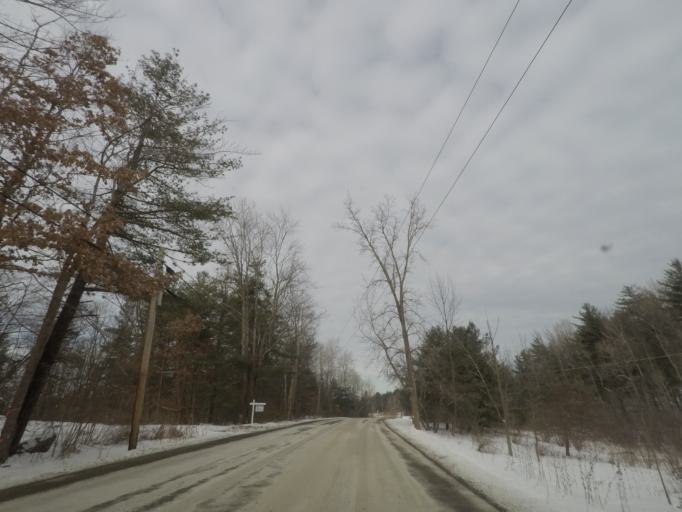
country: US
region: New York
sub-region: Rensselaer County
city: Averill Park
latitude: 42.6182
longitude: -73.5416
